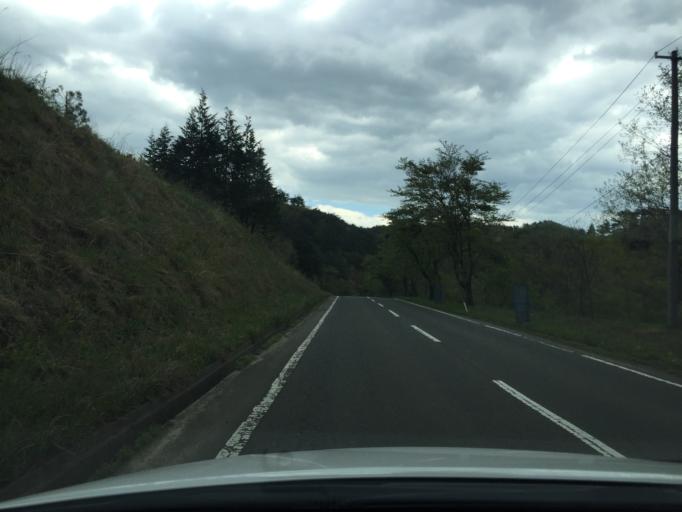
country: JP
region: Fukushima
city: Yanagawamachi-saiwaicho
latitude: 37.7443
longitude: 140.7225
